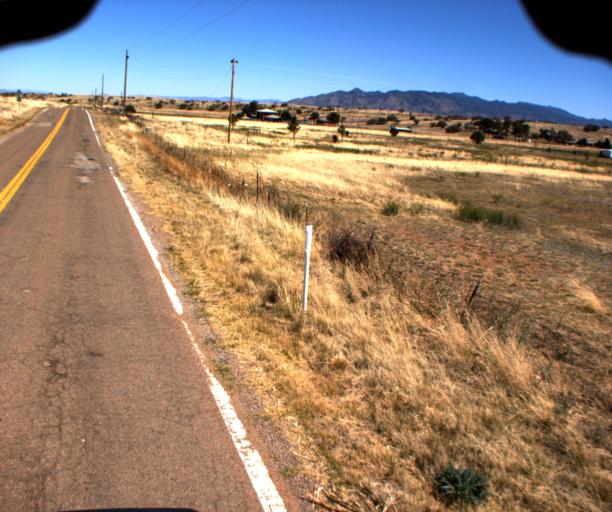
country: US
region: Arizona
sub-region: Cochise County
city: Huachuca City
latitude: 31.6080
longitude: -110.5857
